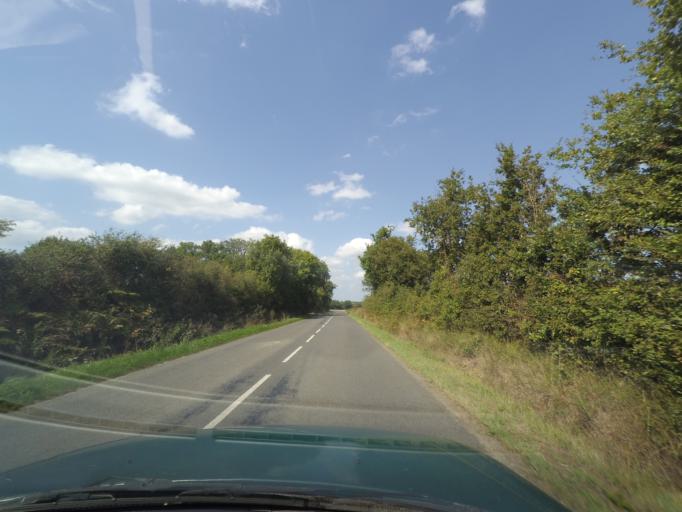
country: FR
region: Pays de la Loire
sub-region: Departement de la Loire-Atlantique
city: Sainte-Pazanne
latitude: 47.0849
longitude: -1.8047
